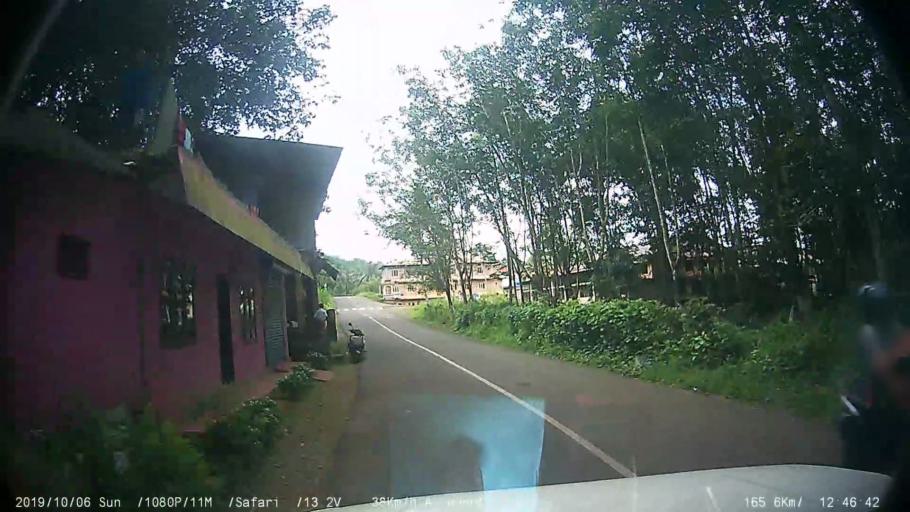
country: IN
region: Kerala
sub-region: Kottayam
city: Palackattumala
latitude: 9.7722
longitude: 76.6058
